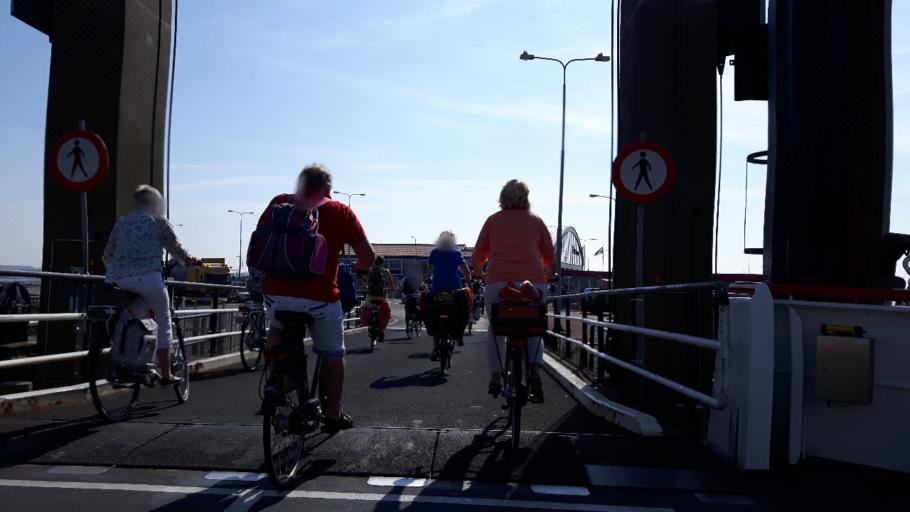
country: NL
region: Friesland
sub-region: Gemeente Dongeradeel
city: Holwerd
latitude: 53.3954
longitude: 5.8791
